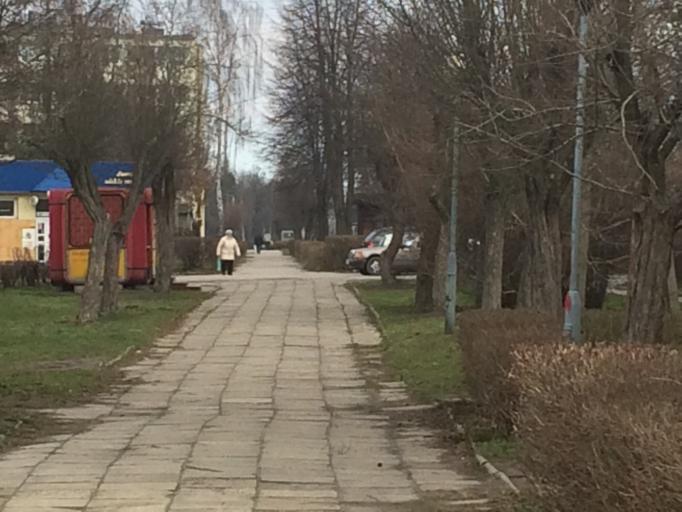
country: PL
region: Swietokrzyskie
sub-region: Powiat starachowicki
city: Starachowice
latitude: 51.0554
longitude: 21.0749
